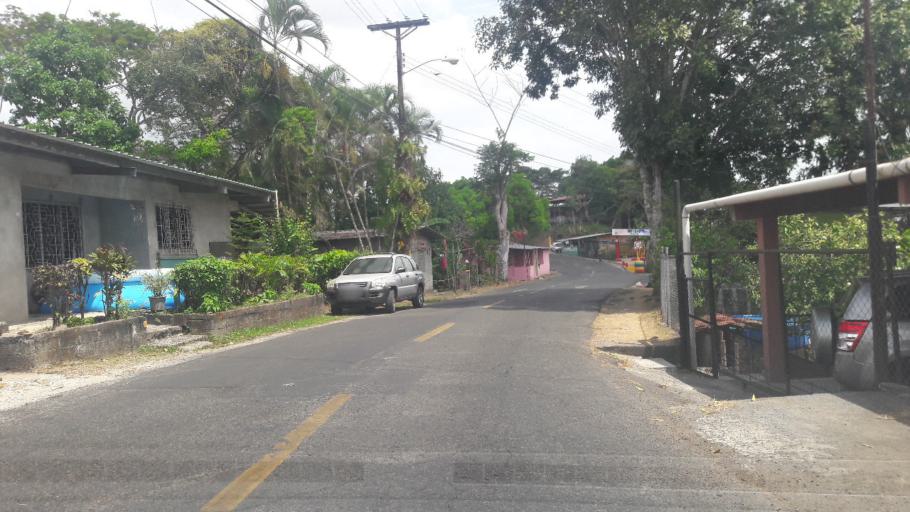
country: PA
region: Panama
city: Alcalde Diaz
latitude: 9.1244
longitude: -79.5566
